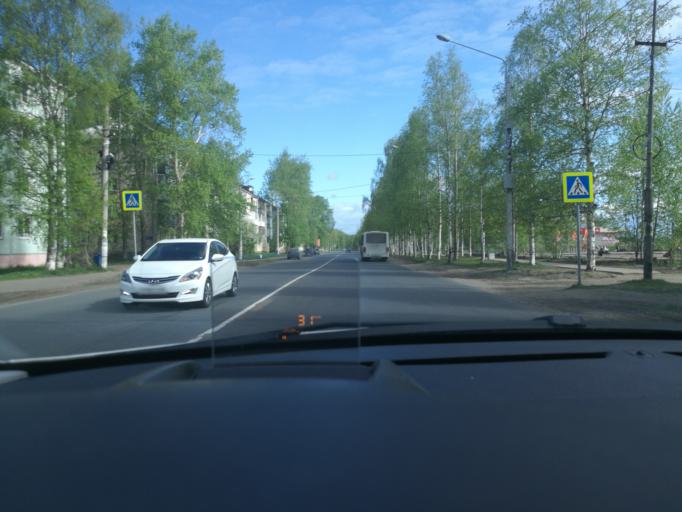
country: RU
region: Arkhangelskaya
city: Arkhangel'sk
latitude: 64.5927
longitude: 40.5901
